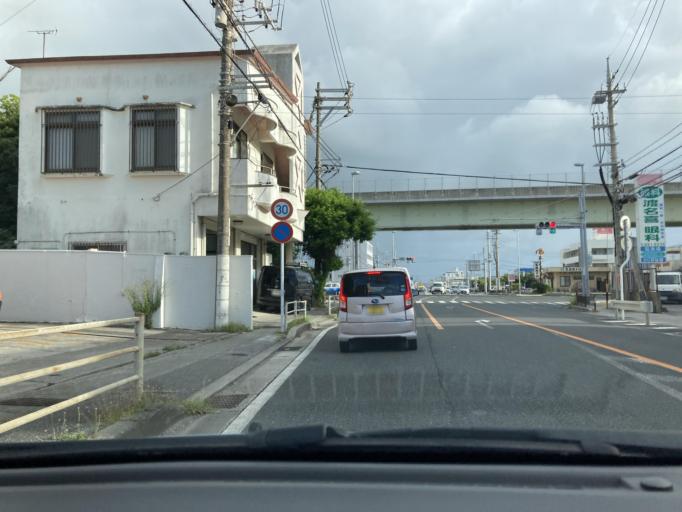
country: JP
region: Okinawa
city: Tomigusuku
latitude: 26.1757
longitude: 127.6658
